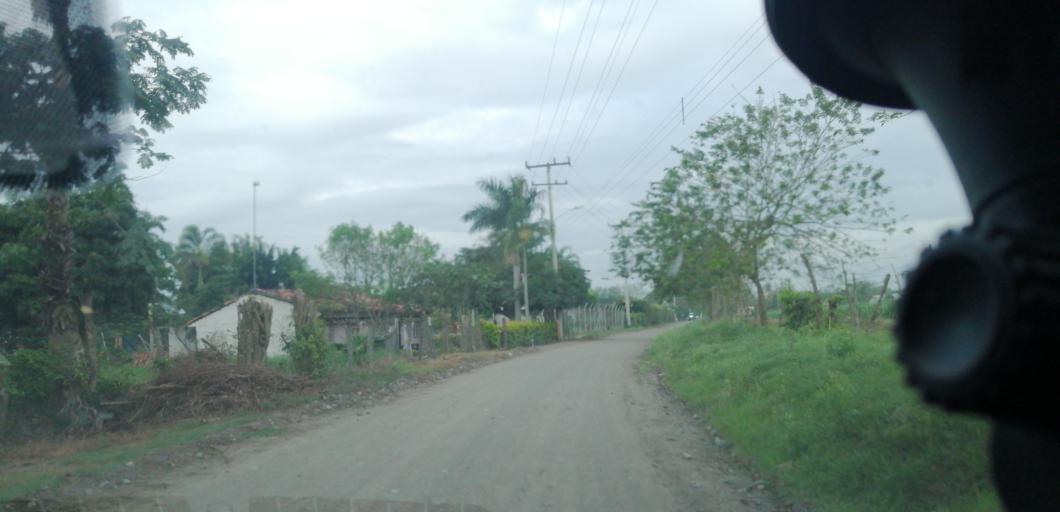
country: CO
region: Valle del Cauca
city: Yumbo
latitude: 3.5719
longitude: -76.3993
